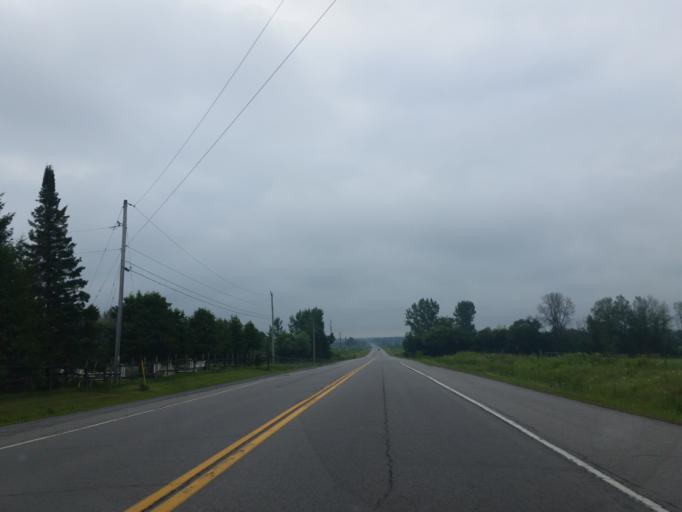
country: CA
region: Ontario
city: Clarence-Rockland
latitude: 45.4149
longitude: -75.4043
